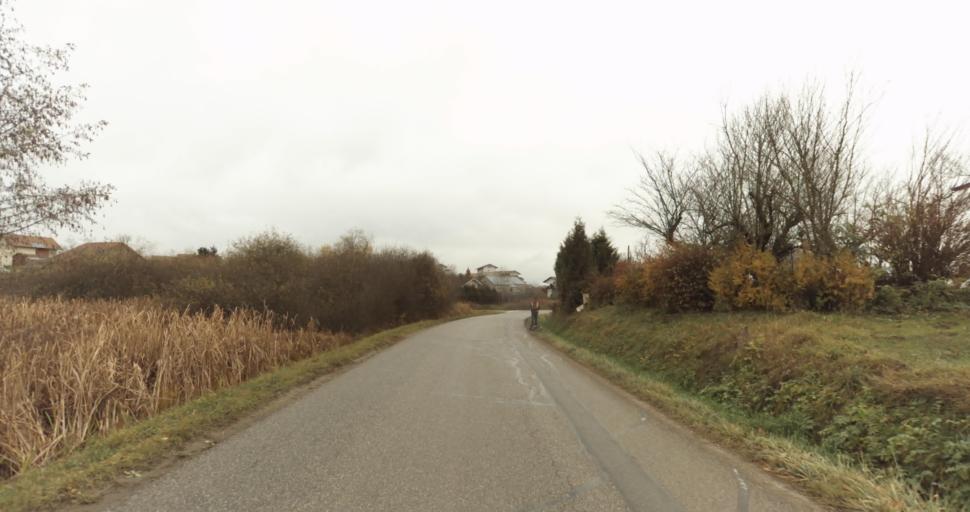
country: FR
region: Rhone-Alpes
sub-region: Departement de la Haute-Savoie
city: Groisy
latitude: 46.0121
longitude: 6.1672
